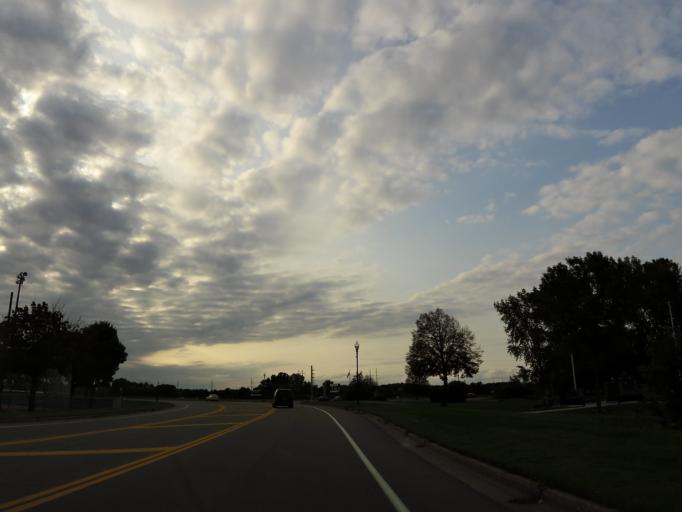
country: US
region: Minnesota
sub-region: Dakota County
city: Farmington
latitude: 44.6410
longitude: -93.1531
